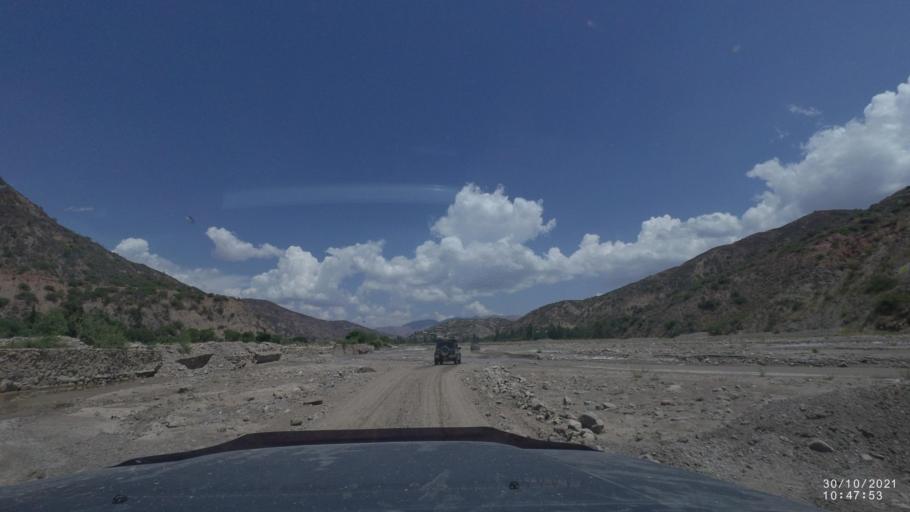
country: BO
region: Cochabamba
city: Sipe Sipe
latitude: -17.5588
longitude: -66.4619
